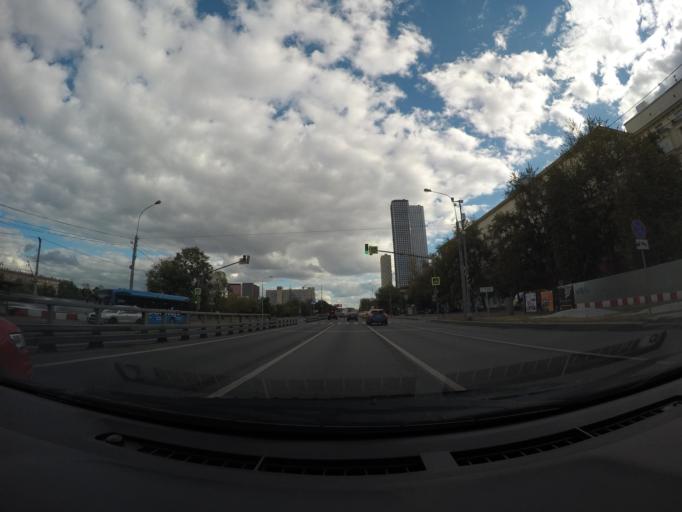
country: RU
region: Moscow
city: Novovladykino
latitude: 55.8134
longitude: 37.5777
